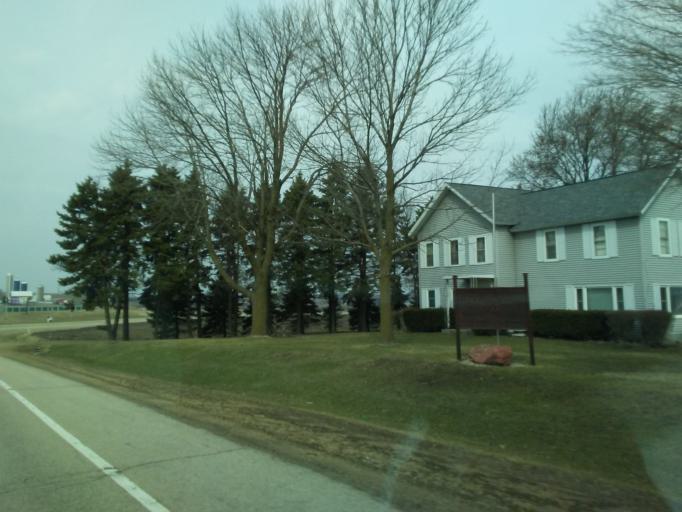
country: US
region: Wisconsin
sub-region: Columbia County
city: Lodi
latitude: 43.2505
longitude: -89.5145
